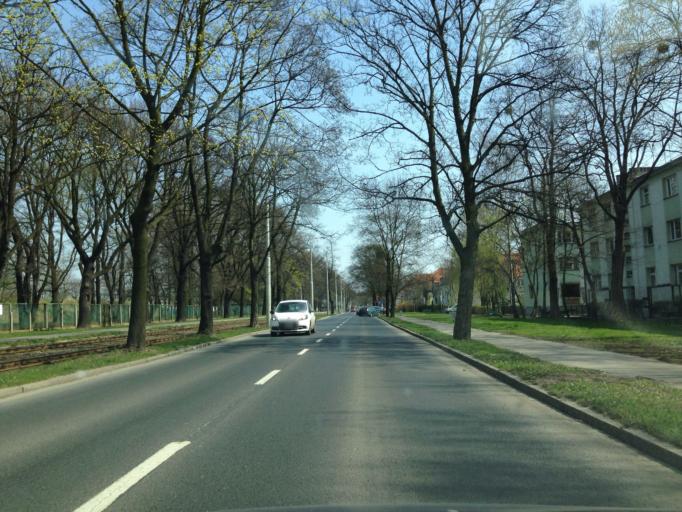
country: PL
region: Lower Silesian Voivodeship
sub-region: Powiat wroclawski
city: Radwanice
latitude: 51.1137
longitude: 17.0940
